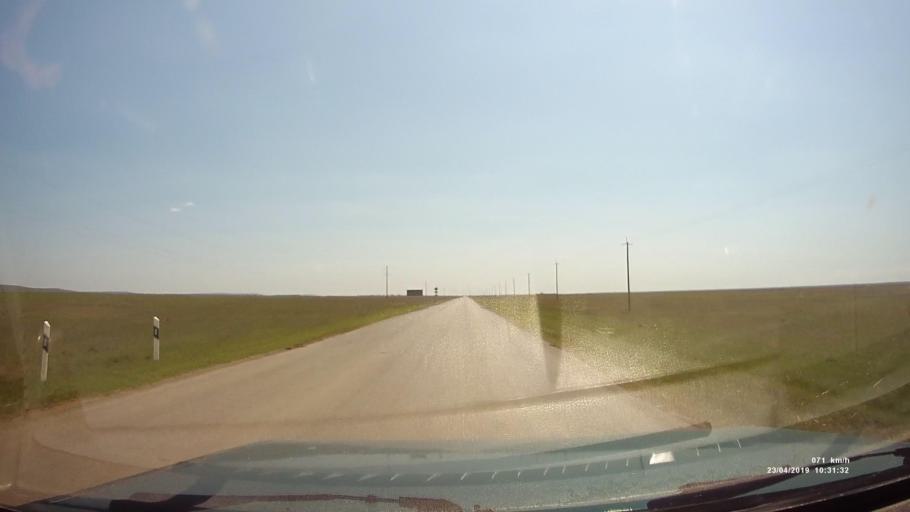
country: RU
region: Kalmykiya
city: Yashalta
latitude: 46.5854
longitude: 42.5633
